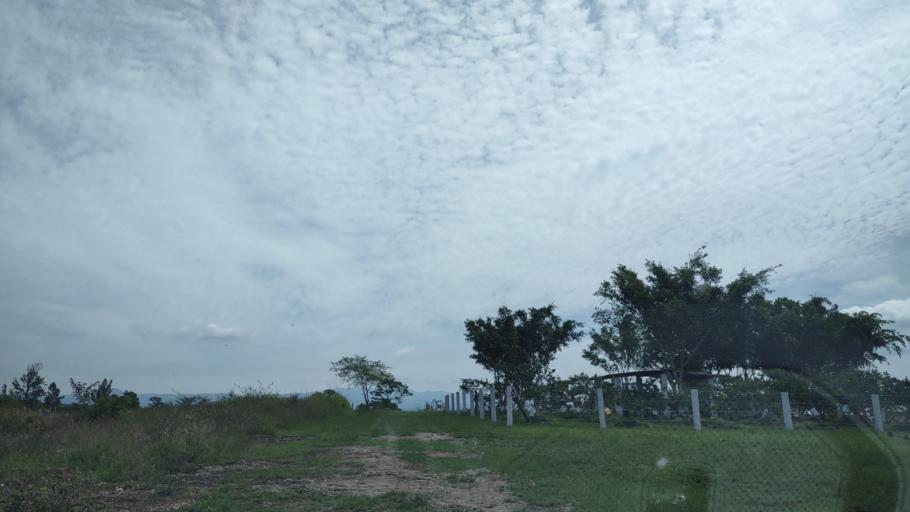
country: MX
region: Veracruz
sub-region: Emiliano Zapata
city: Jacarandas
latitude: 19.4730
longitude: -96.8311
